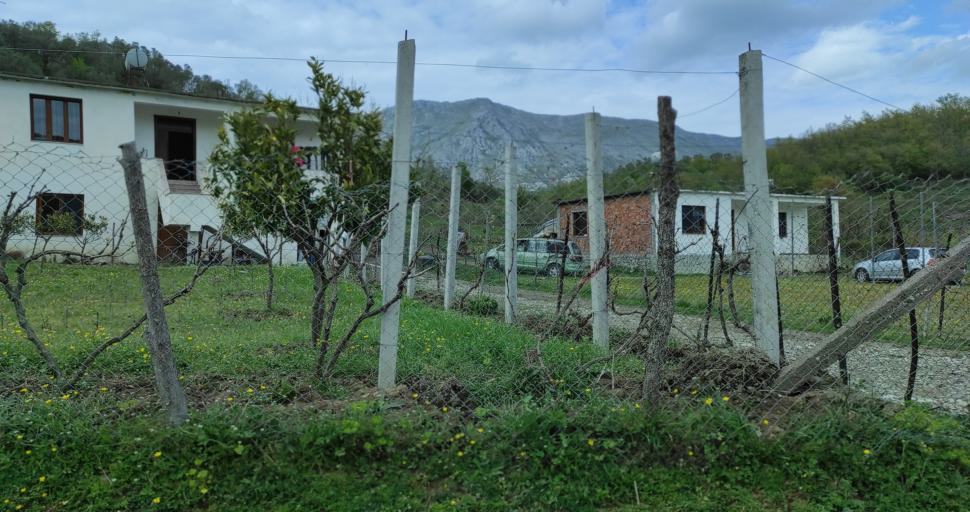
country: AL
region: Shkoder
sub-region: Rrethi i Shkodres
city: Dajc
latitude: 42.0355
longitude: 19.4034
